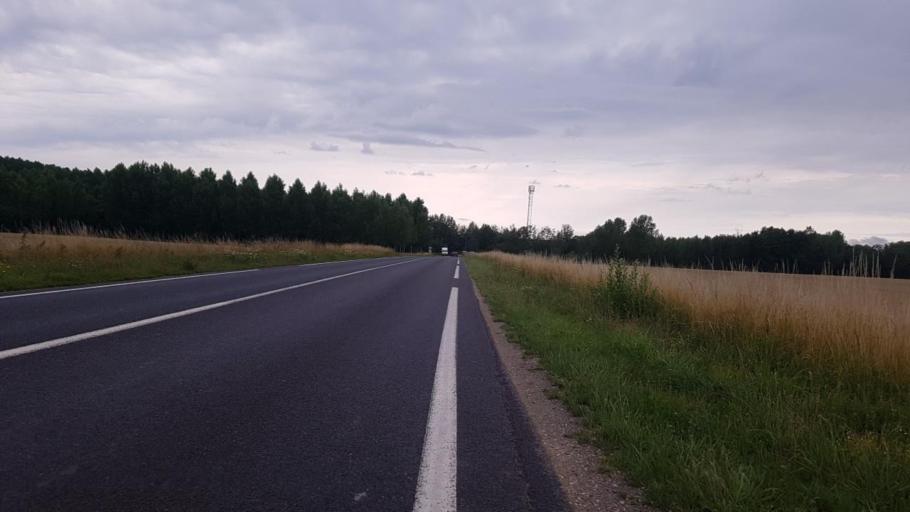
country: FR
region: Champagne-Ardenne
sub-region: Departement de la Marne
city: Vitry-le-Francois
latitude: 48.7533
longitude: 4.7090
